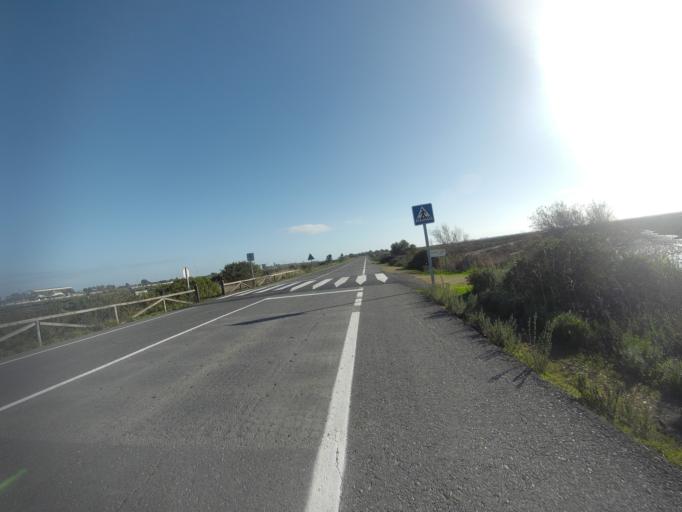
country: ES
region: Andalusia
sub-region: Provincia de Huelva
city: Huelva
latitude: 37.2497
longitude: -6.9680
